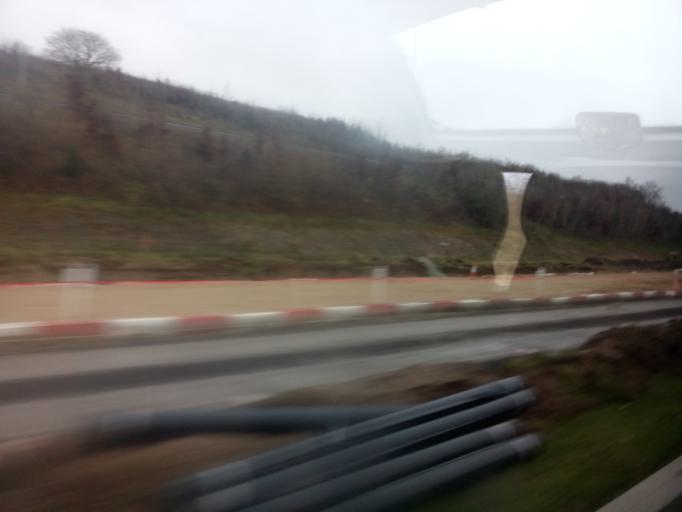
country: GB
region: England
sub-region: Cornwall
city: Liskeard
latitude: 50.4580
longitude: -4.4977
